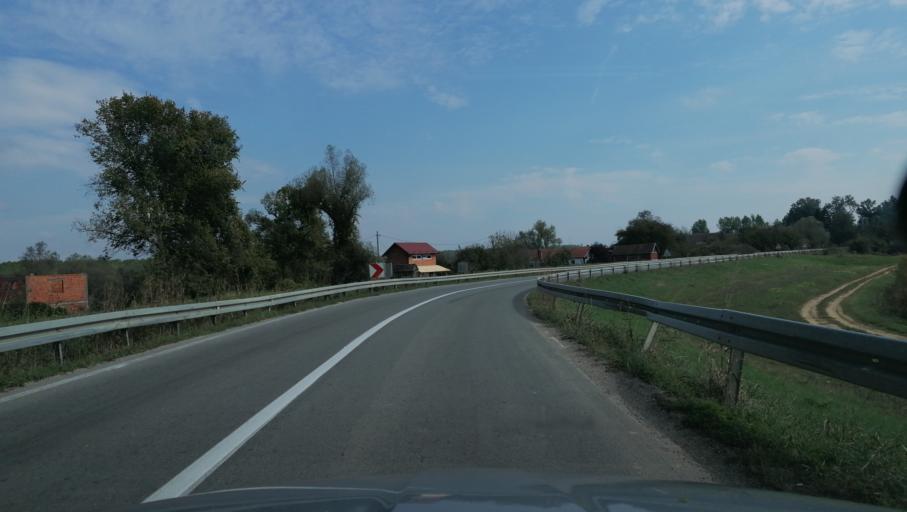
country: BA
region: Republika Srpska
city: Balatun
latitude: 44.8945
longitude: 19.3313
